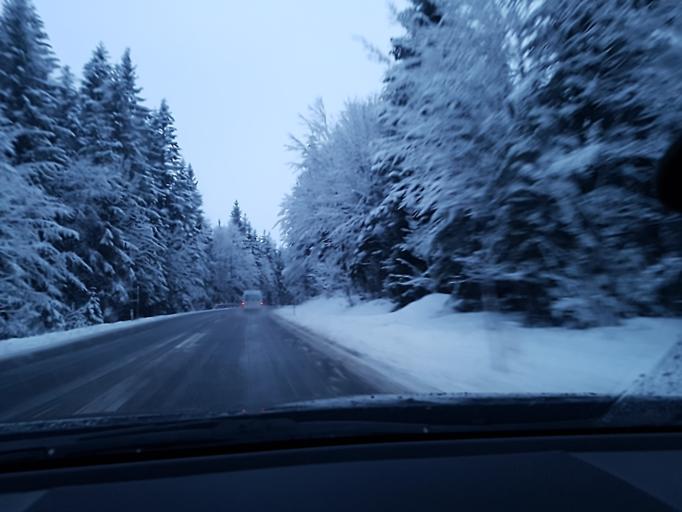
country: AT
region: Upper Austria
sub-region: Politischer Bezirk Gmunden
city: Bad Goisern
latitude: 47.6225
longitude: 13.6803
